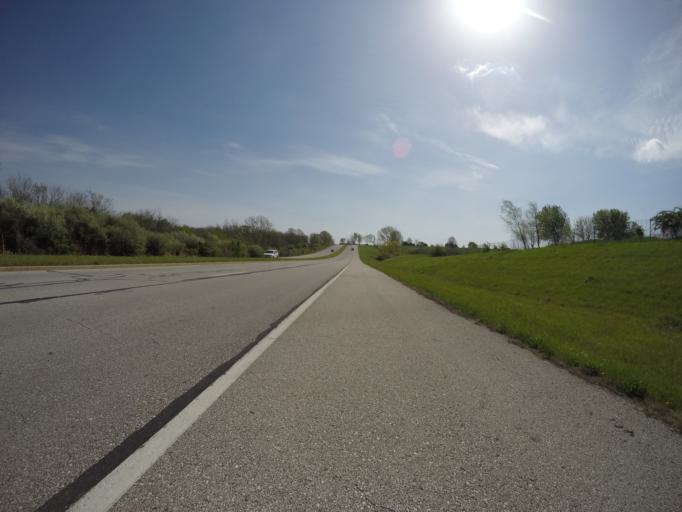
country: US
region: Missouri
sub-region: Jackson County
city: Lees Summit
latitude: 38.9239
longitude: -94.4545
